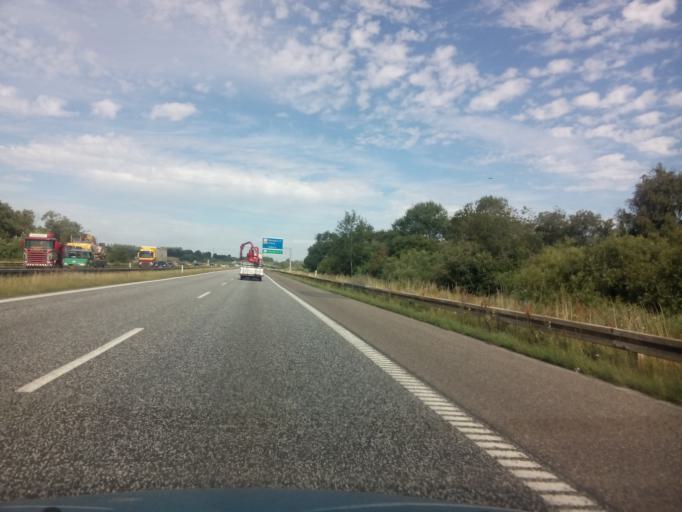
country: DK
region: Central Jutland
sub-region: Randers Kommune
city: Randers
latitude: 56.4516
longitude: 9.9977
